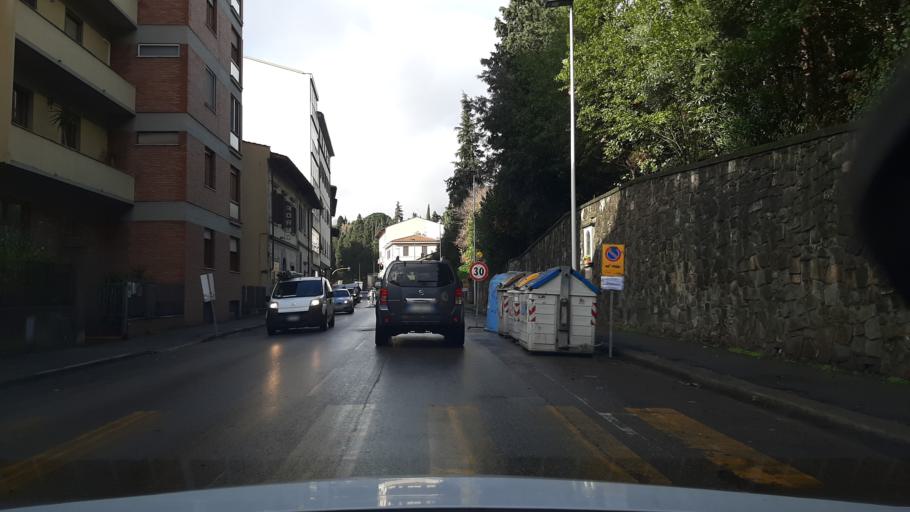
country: IT
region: Tuscany
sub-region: Province of Florence
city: Florence
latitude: 43.7918
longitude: 11.2527
